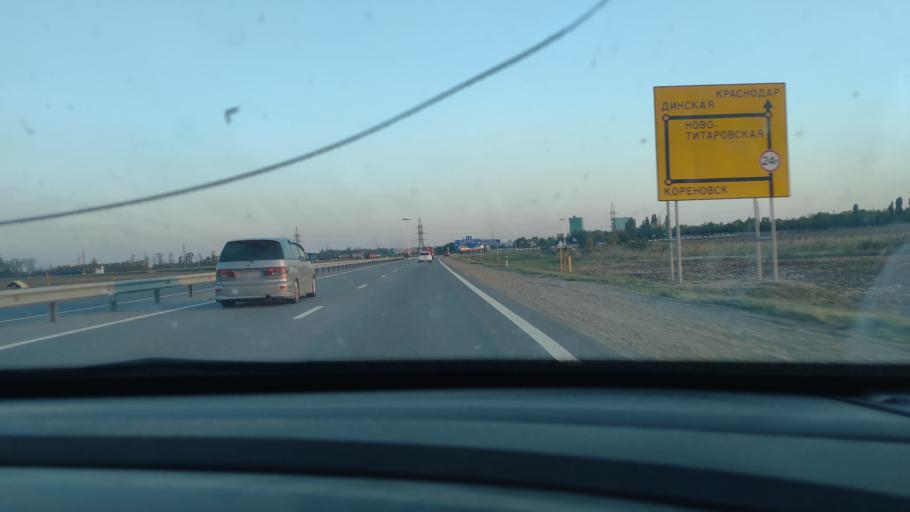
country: RU
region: Krasnodarskiy
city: Timashevsk
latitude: 45.6302
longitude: 38.9833
